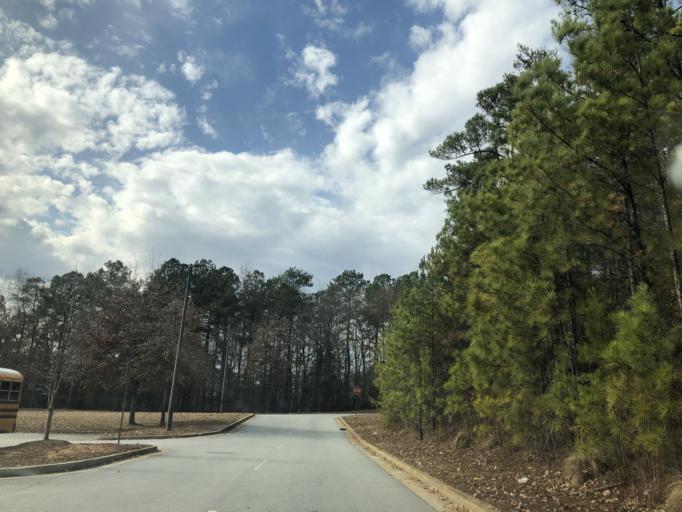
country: US
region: Georgia
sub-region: DeKalb County
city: Panthersville
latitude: 33.6624
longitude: -84.1995
